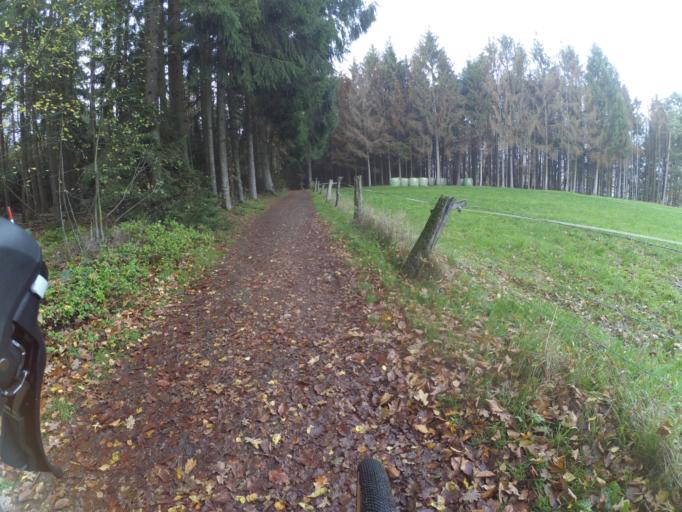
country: DE
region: North Rhine-Westphalia
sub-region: Regierungsbezirk Munster
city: Tecklenburg
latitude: 52.2332
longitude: 7.7559
